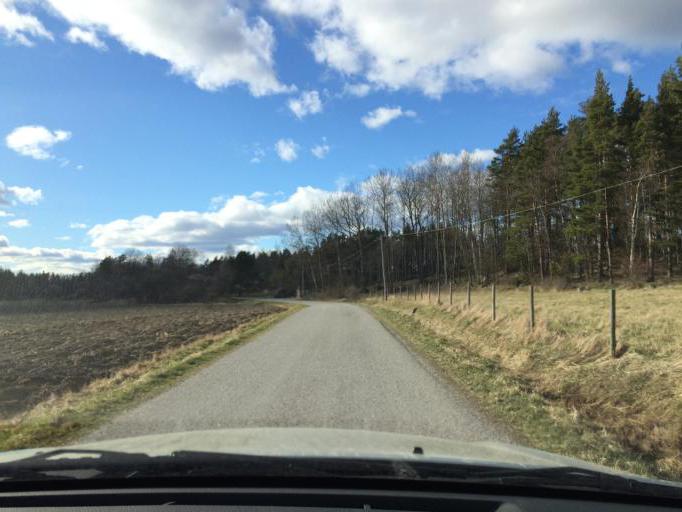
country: SE
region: Soedermanland
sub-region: Eskilstuna Kommun
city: Hallbybrunn
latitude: 59.4305
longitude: 16.3799
